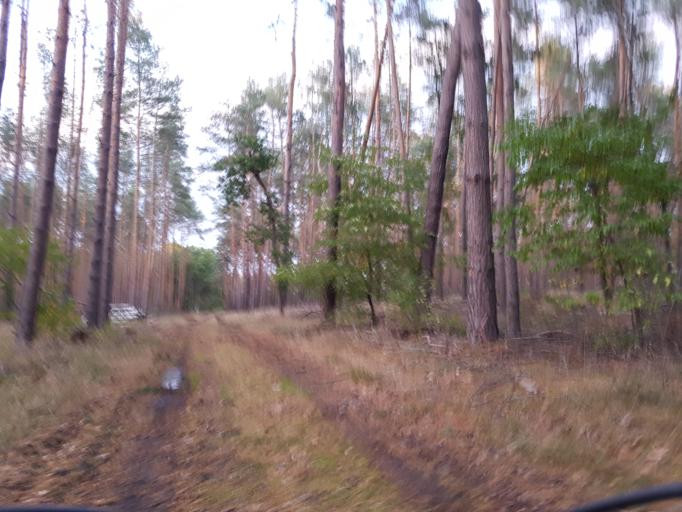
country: DE
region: Brandenburg
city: Schilda
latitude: 51.5993
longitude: 13.3654
